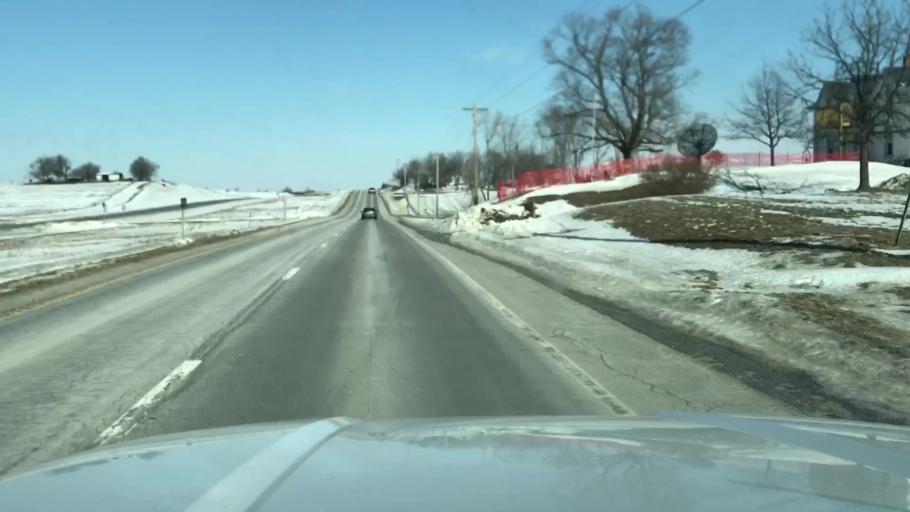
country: US
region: Missouri
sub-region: Andrew County
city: Savannah
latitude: 40.0093
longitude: -94.8796
